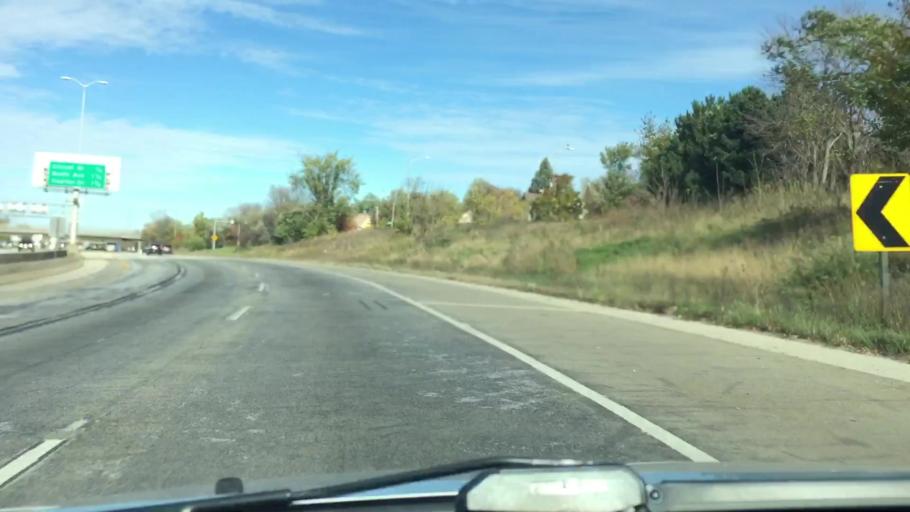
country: US
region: Wisconsin
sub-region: Milwaukee County
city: Milwaukee
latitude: 43.0606
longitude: -87.9206
